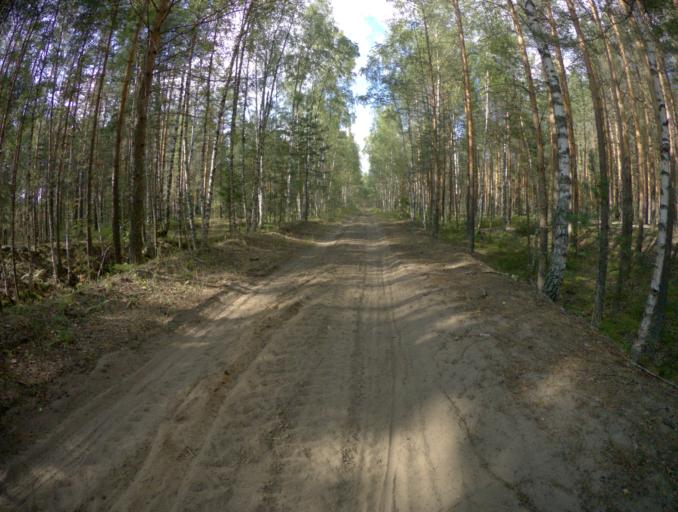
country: RU
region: Vladimir
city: Sobinka
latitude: 55.9488
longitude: 40.0589
